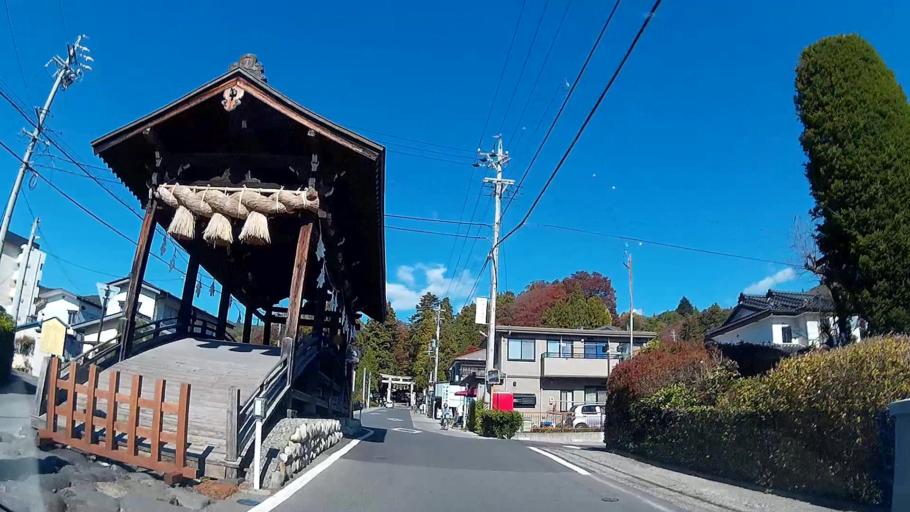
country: JP
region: Nagano
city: Okaya
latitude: 36.0801
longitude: 138.0819
